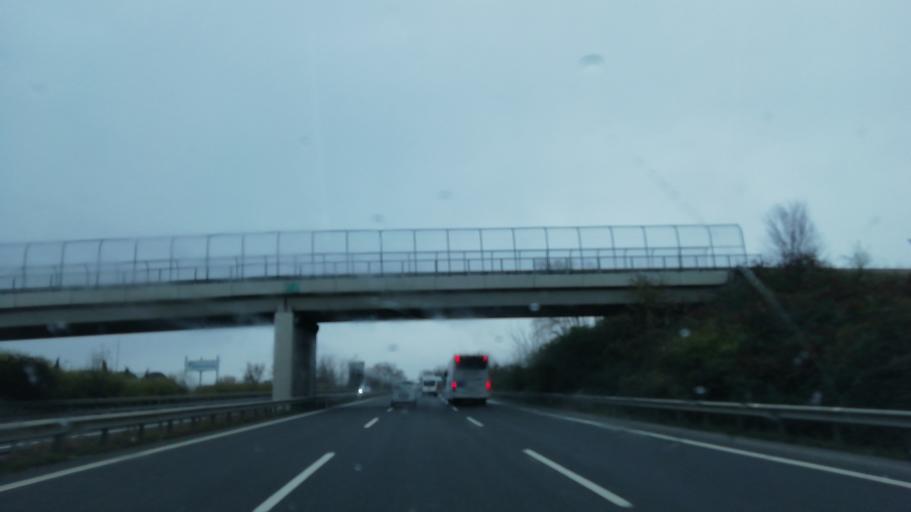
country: TR
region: Sakarya
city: Adapazari
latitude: 40.7160
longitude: 30.3961
